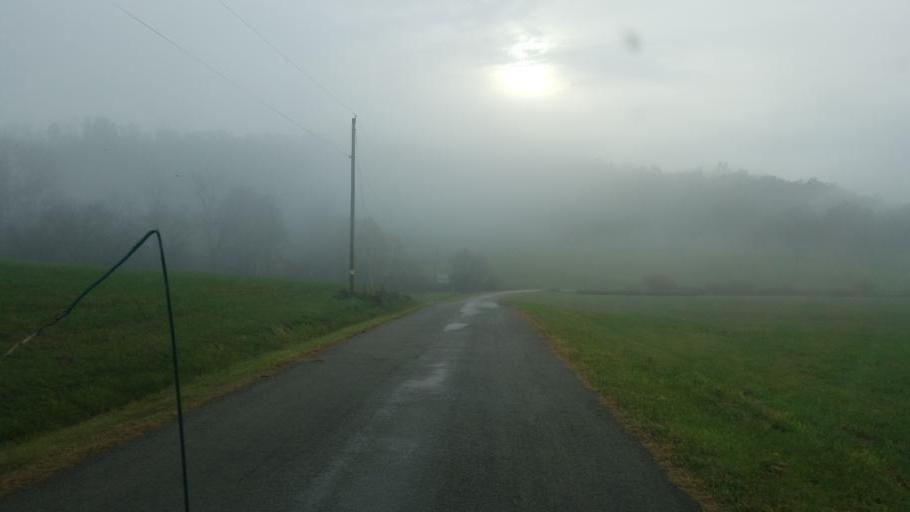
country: US
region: Ohio
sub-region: Athens County
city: Glouster
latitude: 39.4490
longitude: -81.9226
